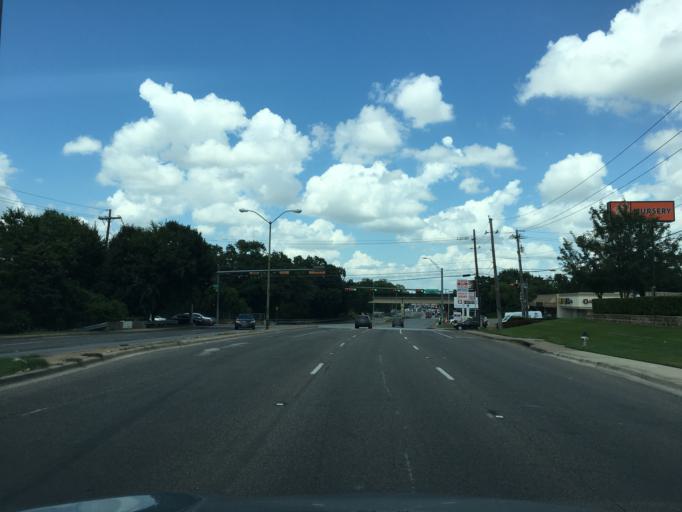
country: US
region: Texas
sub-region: Dallas County
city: Highland Park
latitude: 32.8626
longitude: -96.7499
